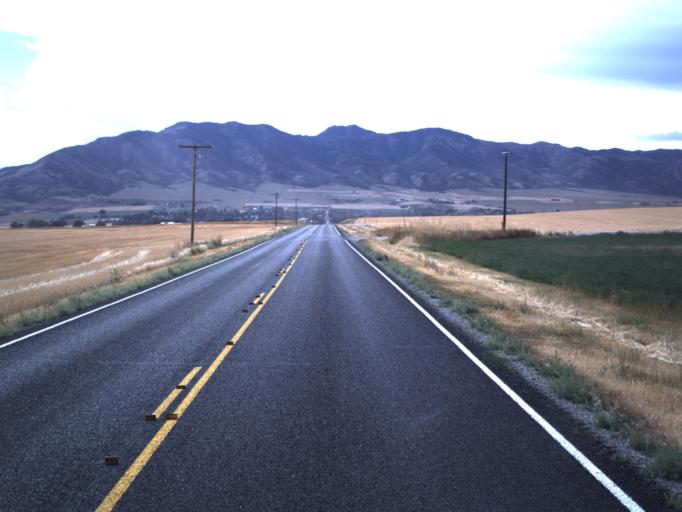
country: US
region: Utah
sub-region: Cache County
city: Benson
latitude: 41.9192
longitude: -112.0096
